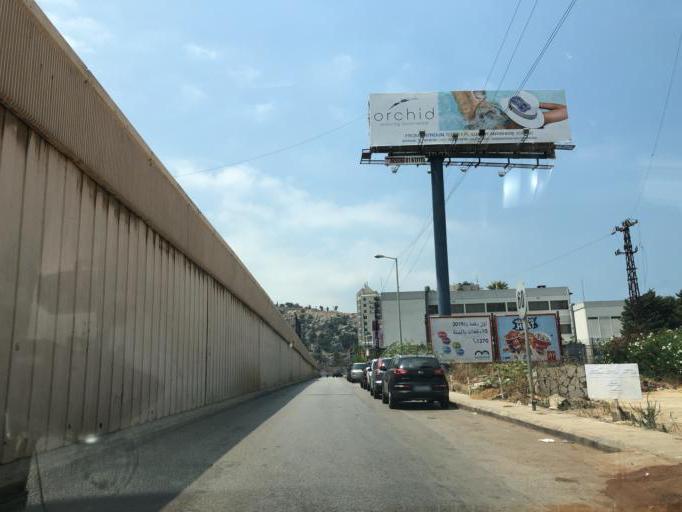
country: LB
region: Mont-Liban
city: Djounie
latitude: 33.9595
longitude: 35.6020
